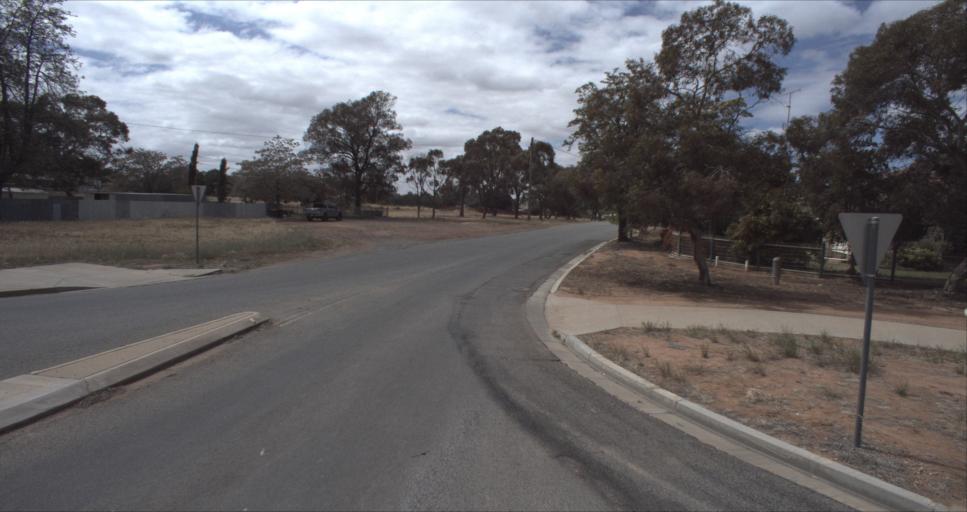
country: AU
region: New South Wales
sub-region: Leeton
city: Leeton
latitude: -34.5570
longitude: 146.4002
